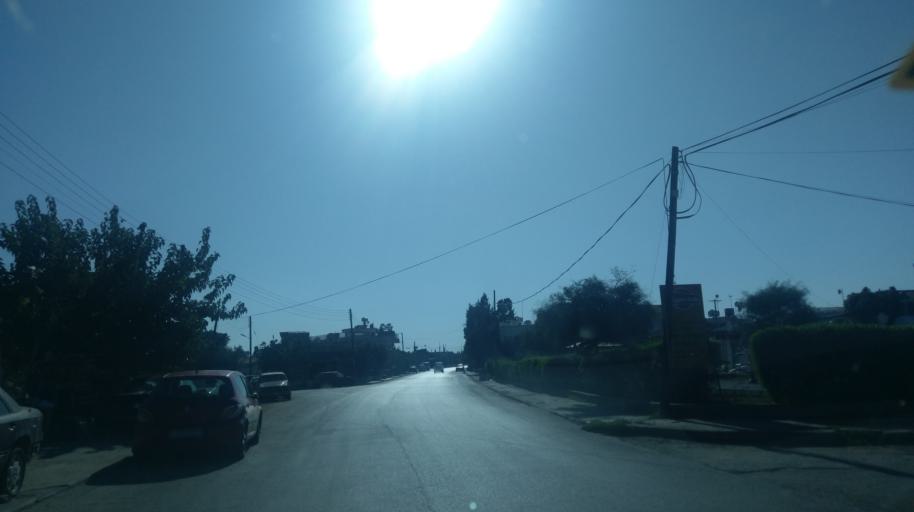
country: CY
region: Ammochostos
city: Famagusta
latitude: 35.1058
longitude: 33.9484
